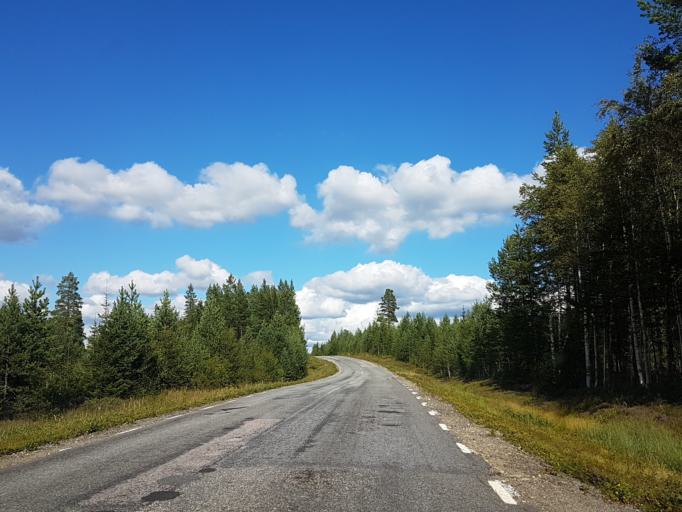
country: SE
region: Vaesterbotten
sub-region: Skelleftea Kommun
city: Burtraesk
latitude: 64.2315
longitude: 20.4710
